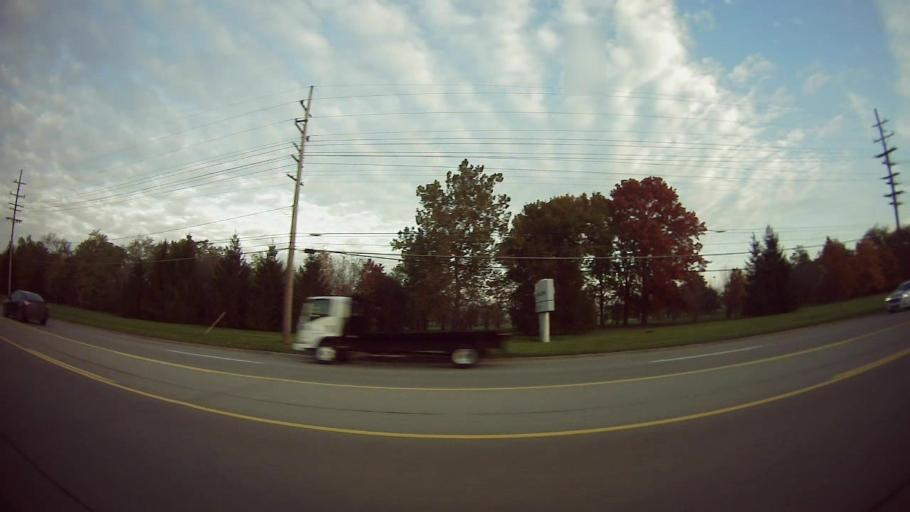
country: US
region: Michigan
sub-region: Macomb County
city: Sterling Heights
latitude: 42.5509
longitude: -83.0381
